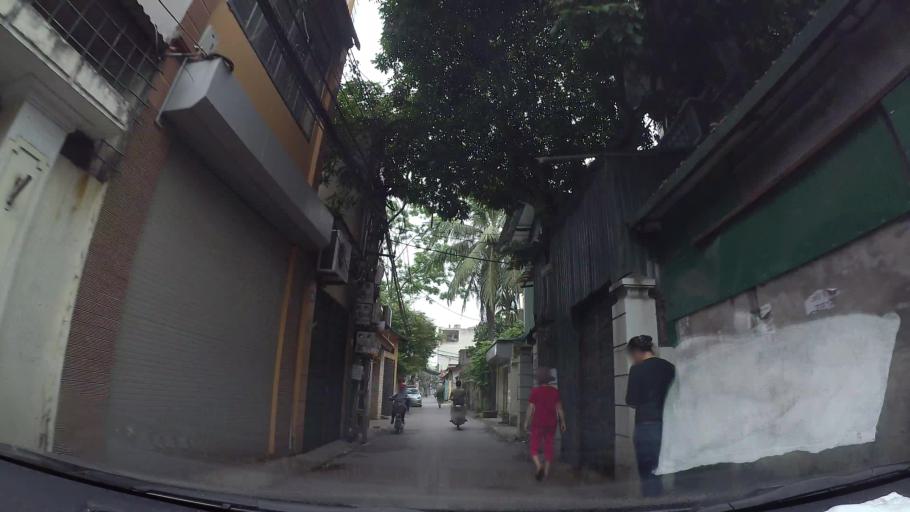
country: VN
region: Hung Yen
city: Van Giang
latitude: 20.9783
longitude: 105.8939
